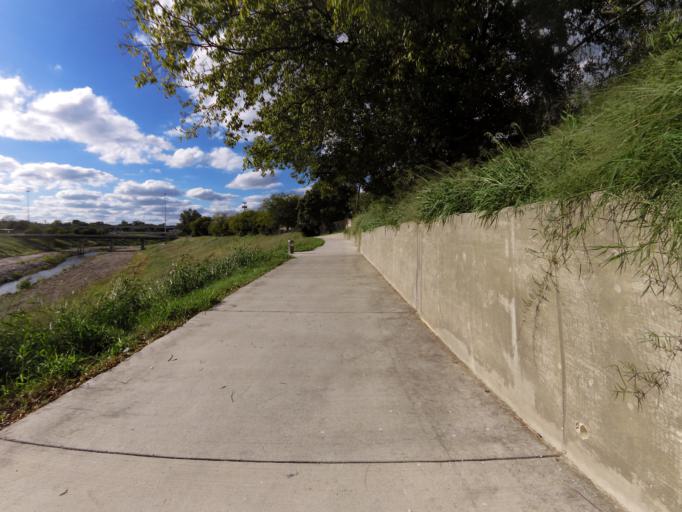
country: US
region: Texas
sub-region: Bexar County
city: San Antonio
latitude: 29.4032
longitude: -98.5069
